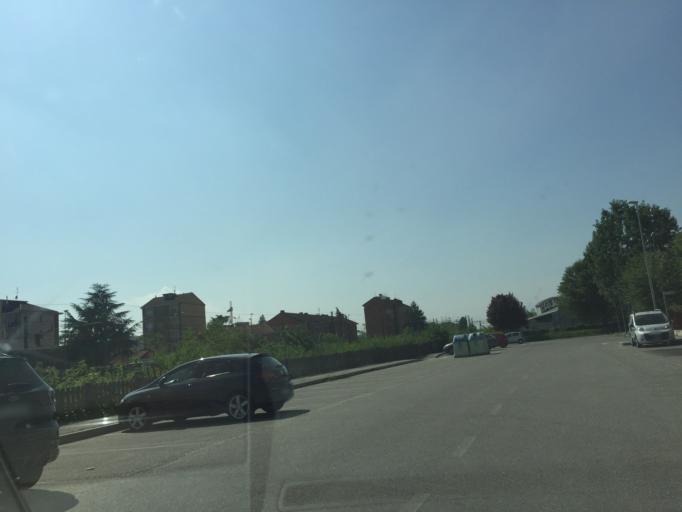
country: IT
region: Piedmont
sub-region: Provincia di Torino
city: Lesna
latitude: 45.0580
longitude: 7.6244
